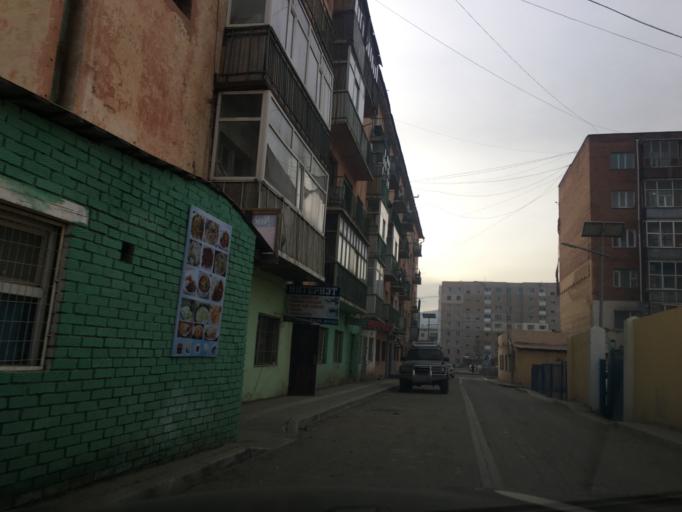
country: MN
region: Ulaanbaatar
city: Ulaanbaatar
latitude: 47.9158
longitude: 106.8877
